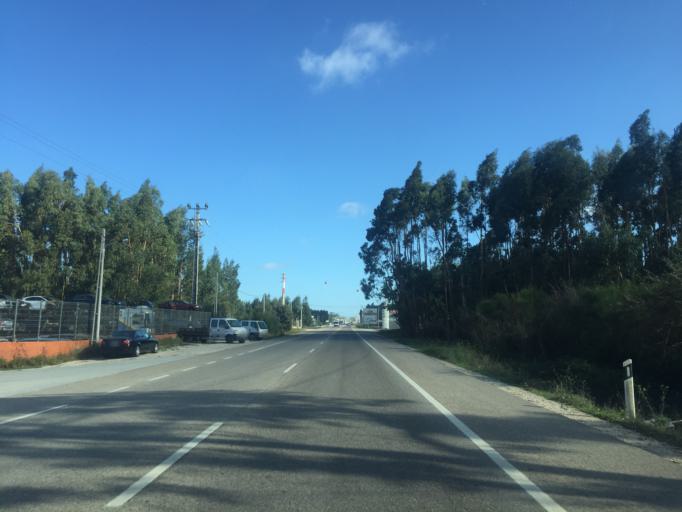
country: PT
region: Leiria
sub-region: Alcobaca
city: Aljubarrota
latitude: 39.5453
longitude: -8.8958
